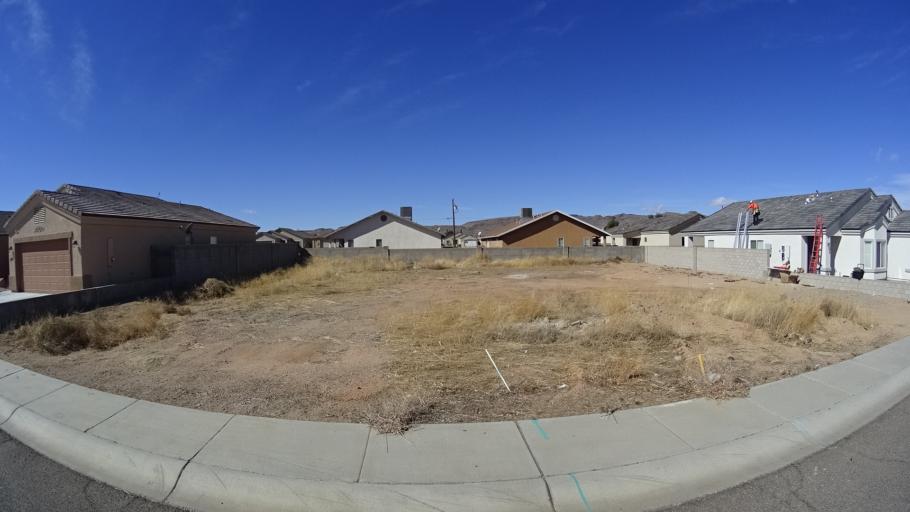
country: US
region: Arizona
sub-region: Mohave County
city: New Kingman-Butler
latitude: 35.2292
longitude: -114.0217
